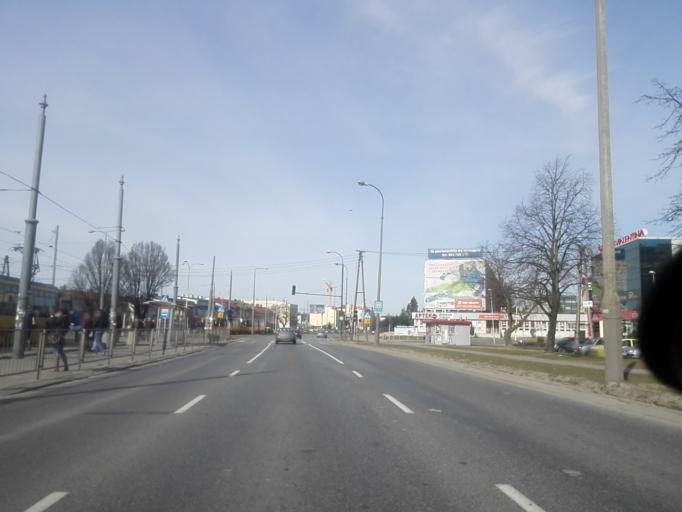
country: PL
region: Masovian Voivodeship
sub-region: Warszawa
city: Wlochy
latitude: 52.1759
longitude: 20.9447
